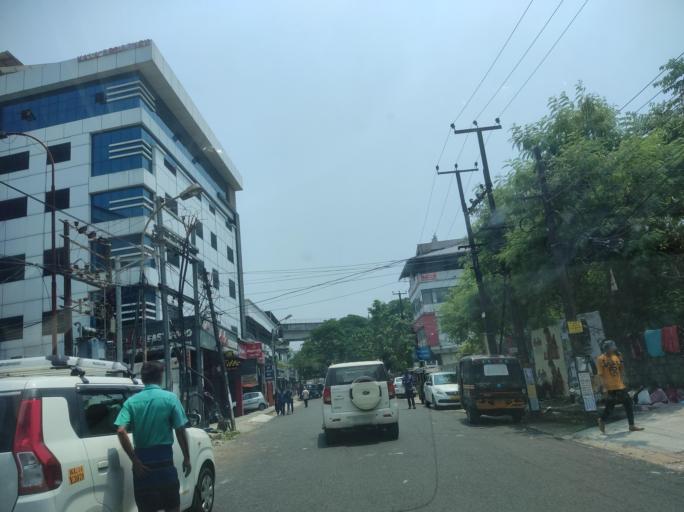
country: IN
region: Kerala
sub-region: Ernakulam
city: Cochin
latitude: 9.9895
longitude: 76.2853
